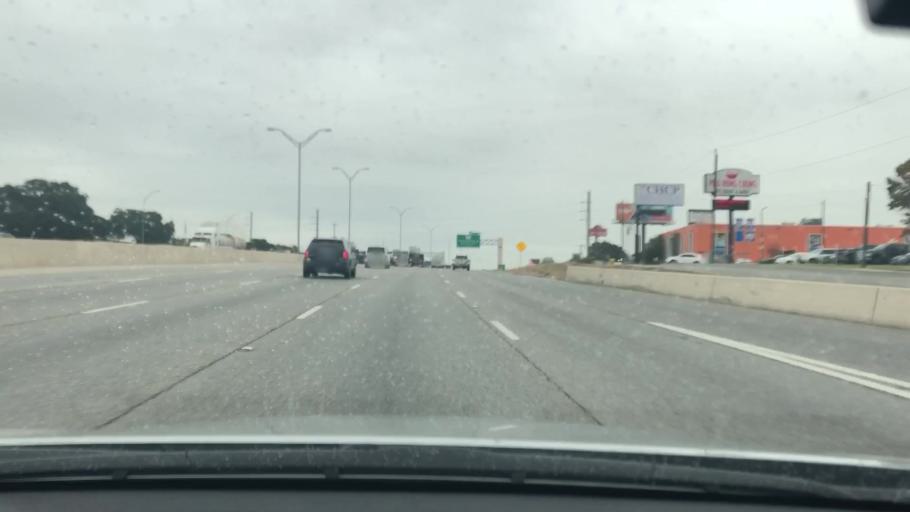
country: US
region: Texas
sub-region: Bexar County
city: Balcones Heights
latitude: 29.4893
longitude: -98.5782
